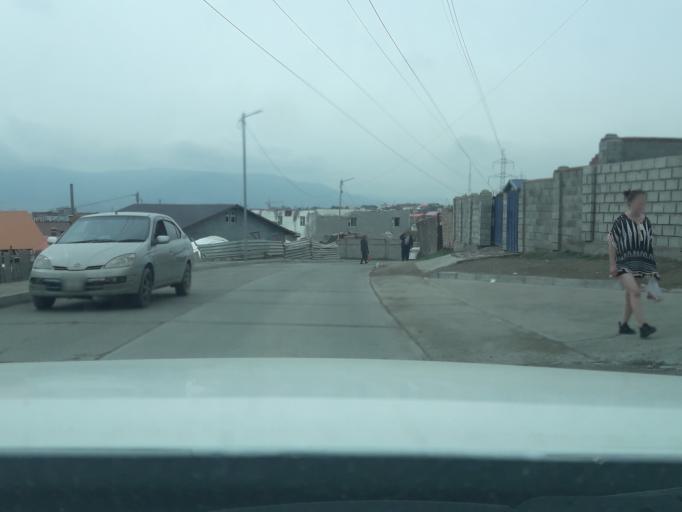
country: MN
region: Ulaanbaatar
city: Ulaanbaatar
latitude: 47.9480
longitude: 106.9042
